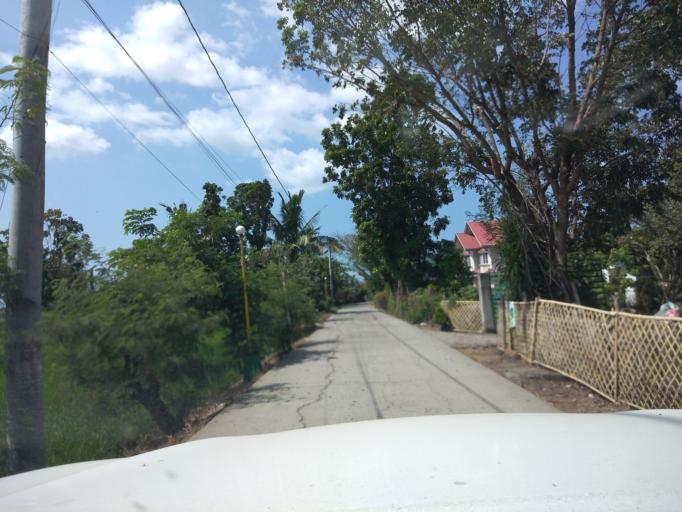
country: PH
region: Central Luzon
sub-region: Province of Pampanga
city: Bahay Pare
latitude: 15.0463
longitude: 120.8836
